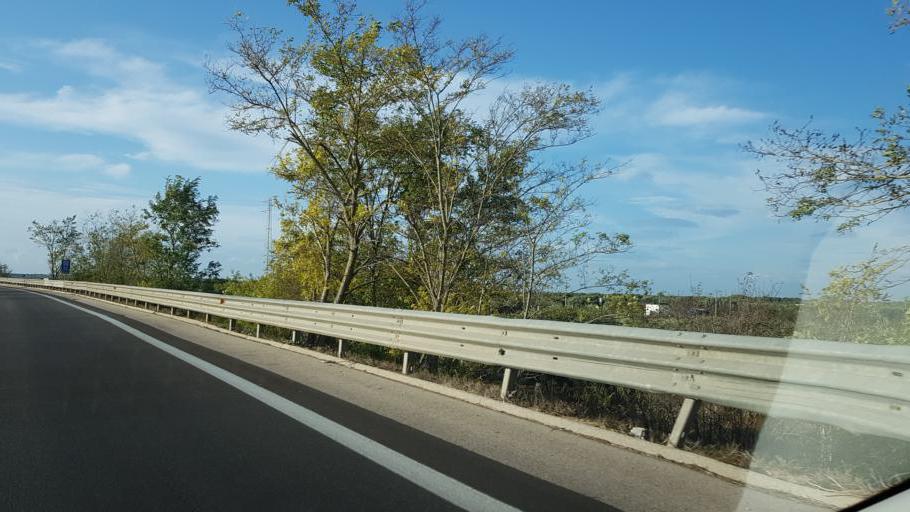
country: IT
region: Apulia
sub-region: Provincia di Brindisi
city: Francavilla Fontana
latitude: 40.5449
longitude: 17.5969
